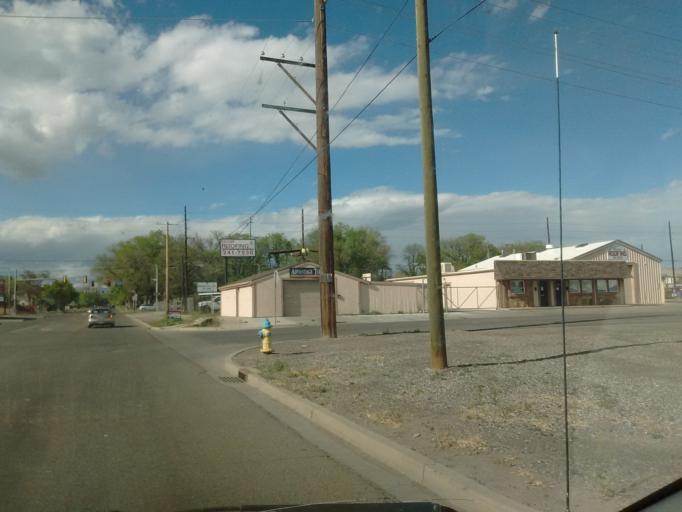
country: US
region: Colorado
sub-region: Mesa County
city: Grand Junction
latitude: 39.0632
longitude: -108.5577
